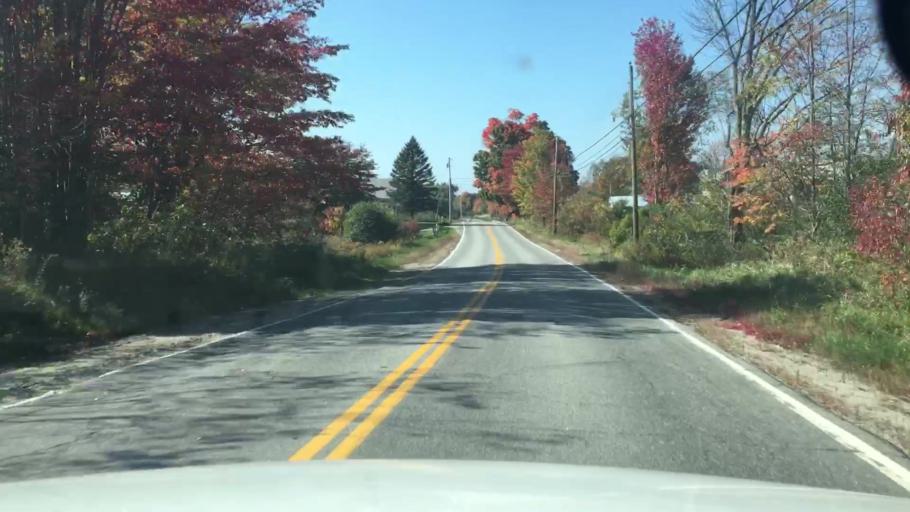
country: US
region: Maine
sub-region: Androscoggin County
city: Lisbon Falls
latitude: 44.0402
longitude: -70.0009
